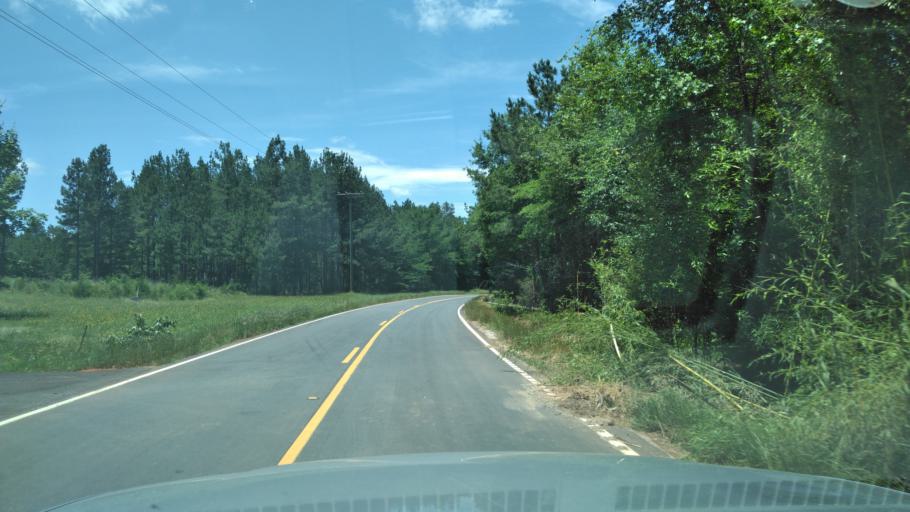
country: US
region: South Carolina
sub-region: Greenwood County
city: Ware Shoals
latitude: 34.3966
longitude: -82.1205
